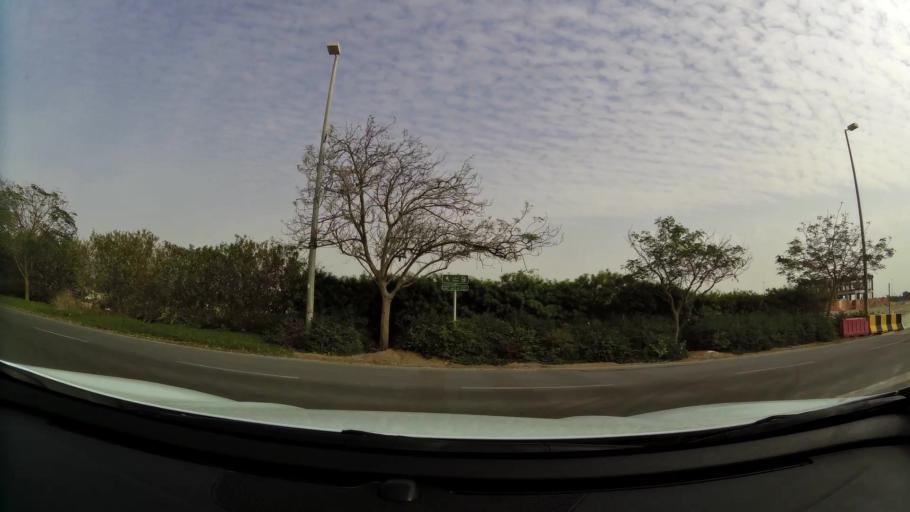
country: AE
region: Abu Dhabi
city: Abu Dhabi
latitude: 24.5958
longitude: 54.7019
